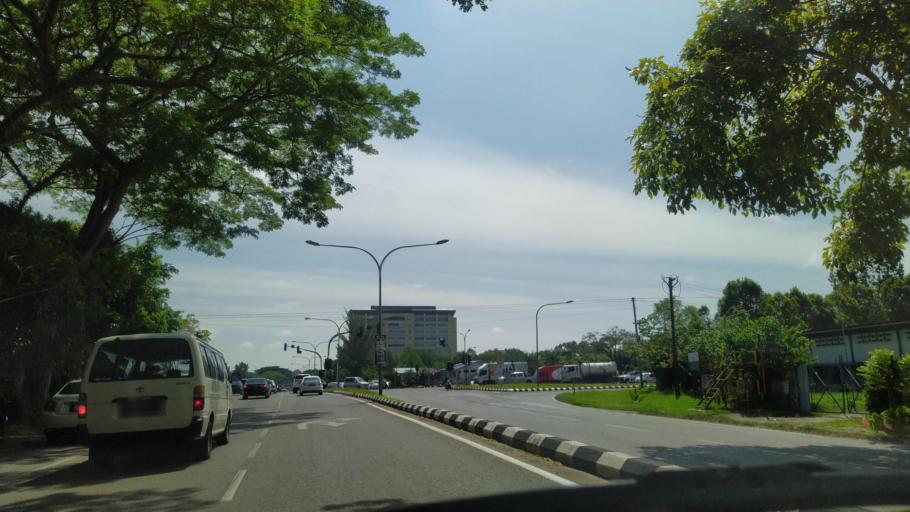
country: MY
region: Sarawak
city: Sibu
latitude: 2.3195
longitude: 111.8389
